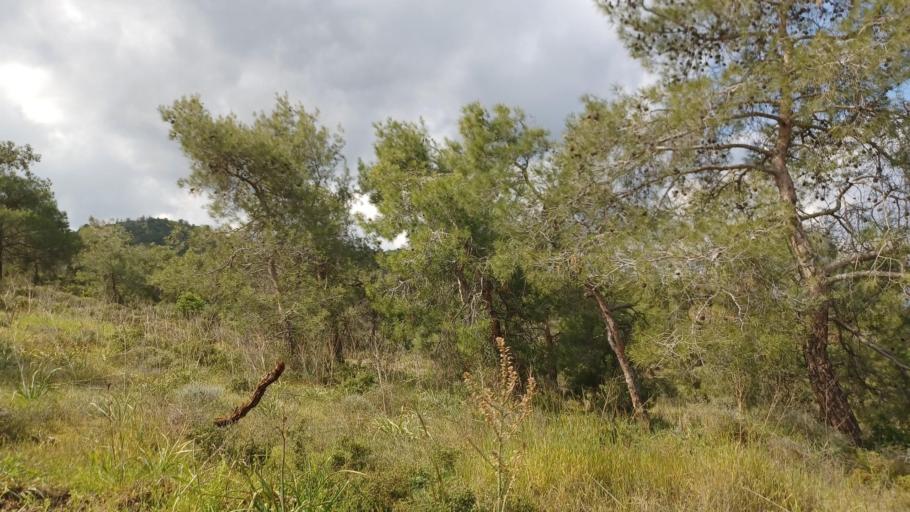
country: CY
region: Lefkosia
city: Astromeritis
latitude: 35.0742
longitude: 32.9625
